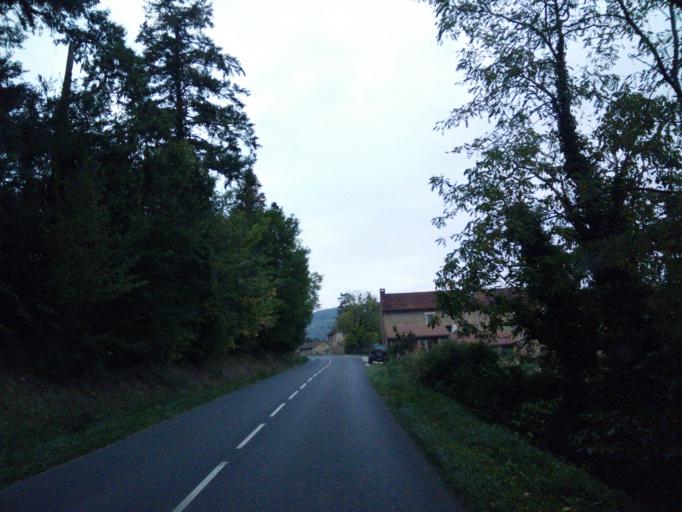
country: FR
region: Aquitaine
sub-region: Departement de la Dordogne
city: Carsac-Aillac
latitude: 44.8347
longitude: 1.2749
